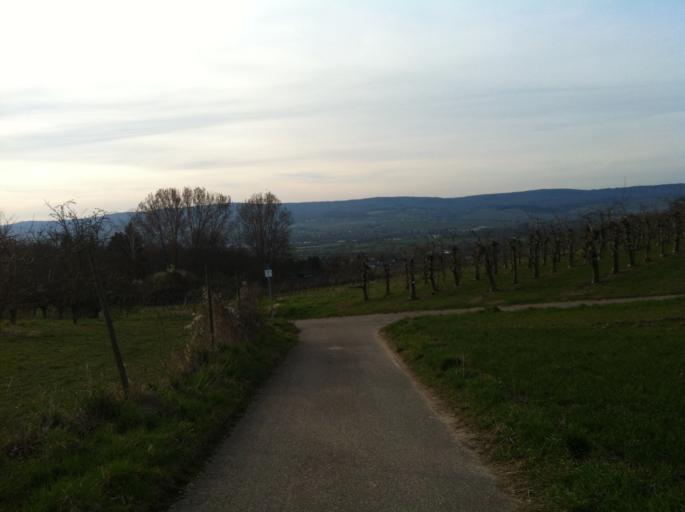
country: DE
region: Rheinland-Pfalz
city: Wackernheim
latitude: 49.9907
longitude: 8.1380
